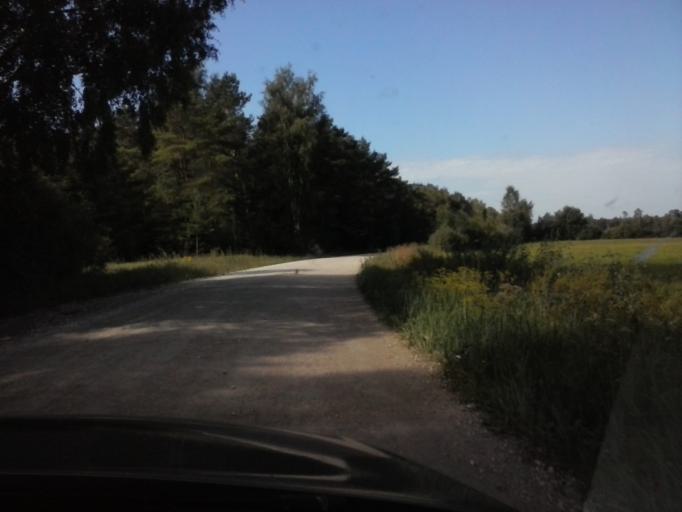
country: EE
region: Laeaene
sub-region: Ridala Parish
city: Uuemoisa
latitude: 58.8815
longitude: 23.5932
